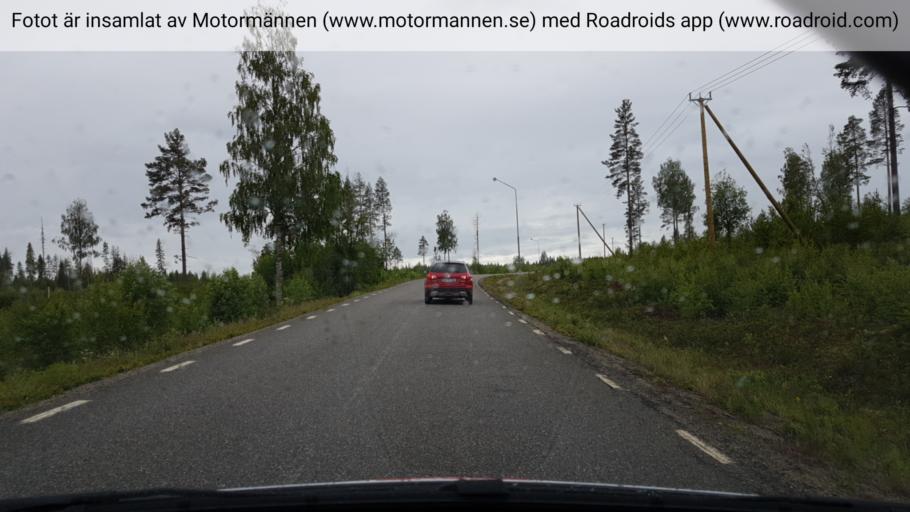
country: SE
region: Vaesterbotten
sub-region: Bjurholms Kommun
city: Bjurholm
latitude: 64.1374
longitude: 19.3099
